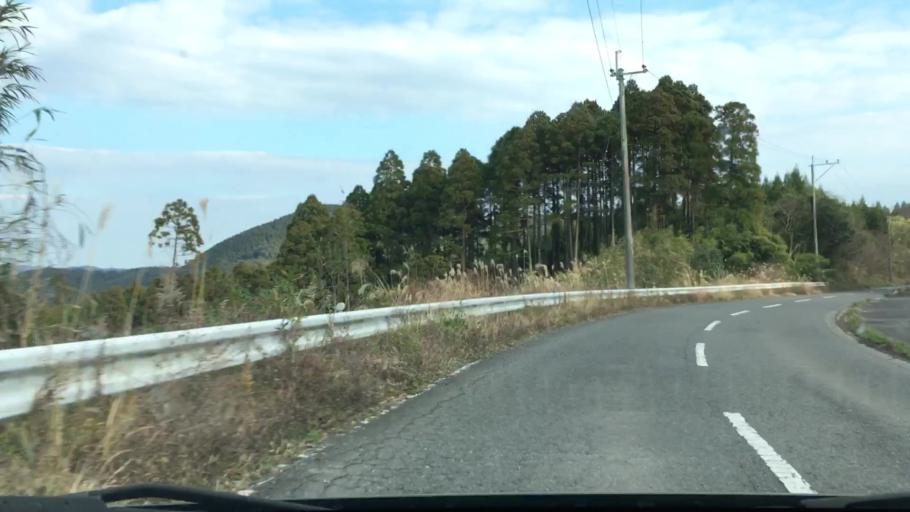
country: JP
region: Miyazaki
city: Nichinan
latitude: 31.6102
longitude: 131.3313
